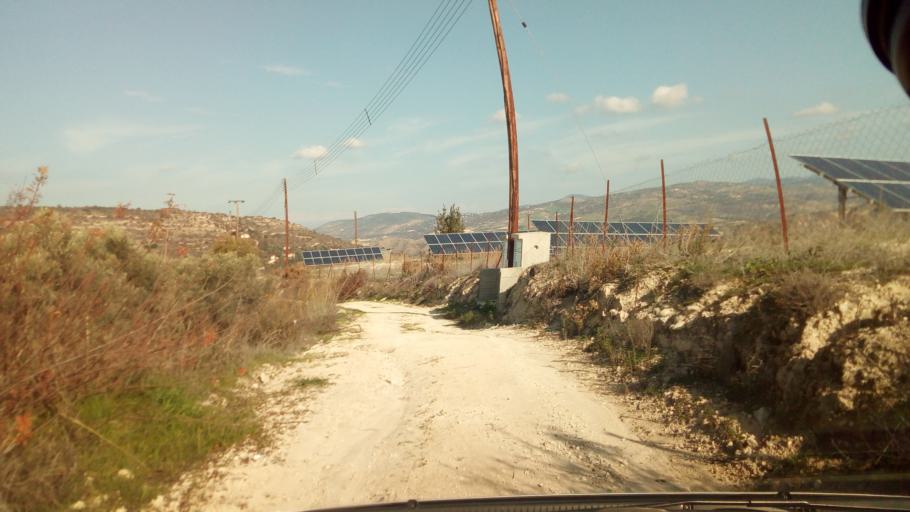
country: CY
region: Pafos
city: Pegeia
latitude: 34.9298
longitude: 32.4591
